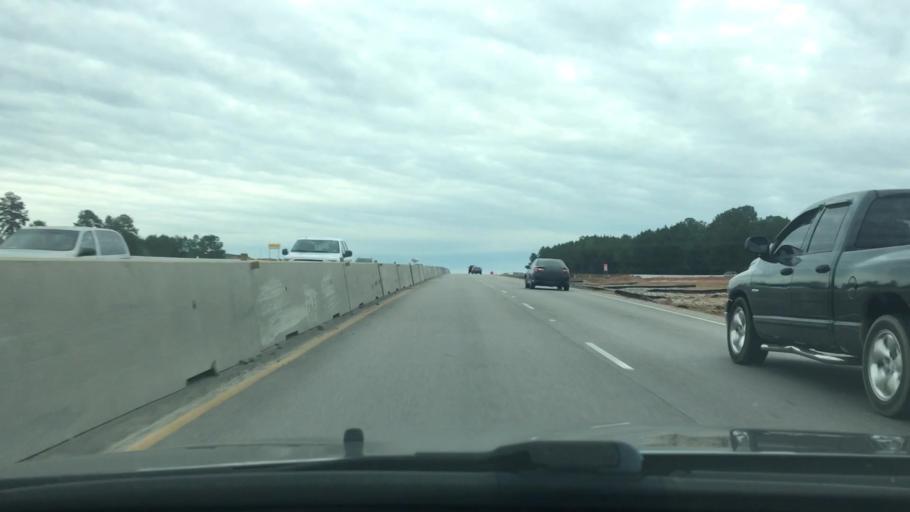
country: US
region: Texas
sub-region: Walker County
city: Huntsville
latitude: 30.6797
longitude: -95.5256
